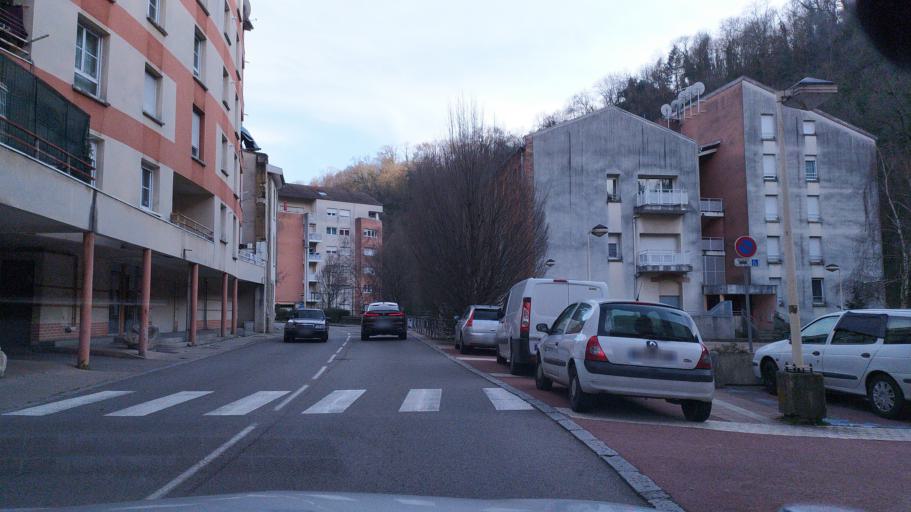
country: FR
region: Rhone-Alpes
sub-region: Departement de l'Isere
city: Vienne
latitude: 45.5258
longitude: 4.8845
